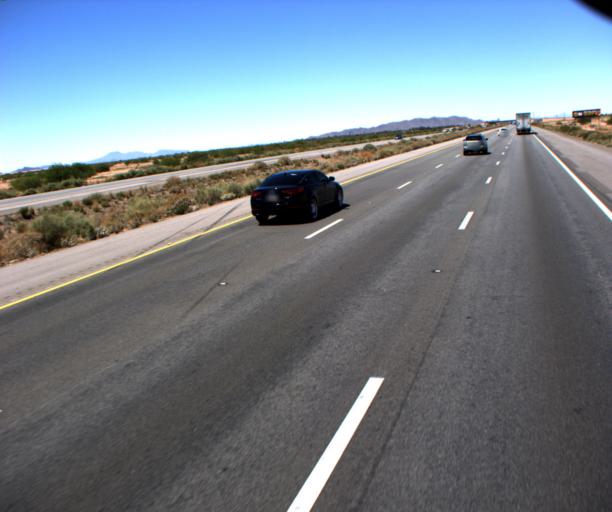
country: US
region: Arizona
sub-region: Pinal County
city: Eloy
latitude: 32.7567
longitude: -111.5860
